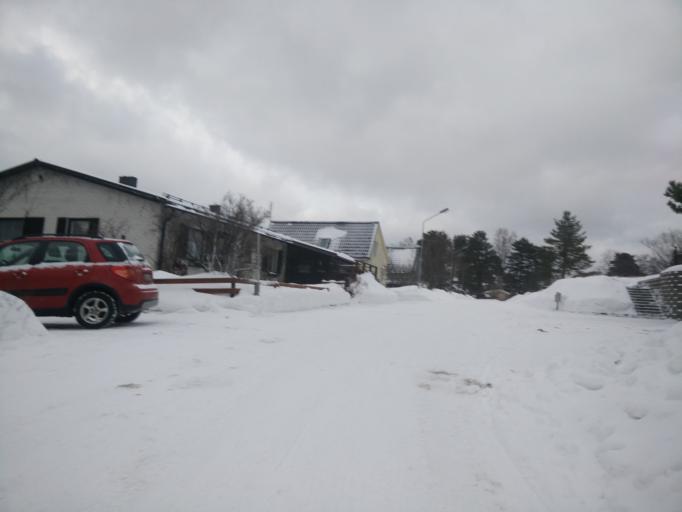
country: SE
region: Vaesternorrland
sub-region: Sundsvalls Kommun
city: Nolby
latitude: 62.2879
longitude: 17.3613
